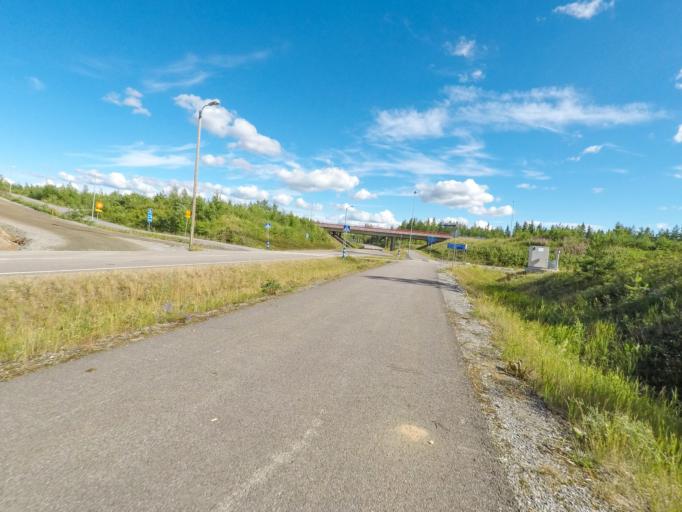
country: FI
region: South Karelia
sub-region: Lappeenranta
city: Joutseno
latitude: 61.1505
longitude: 28.6140
